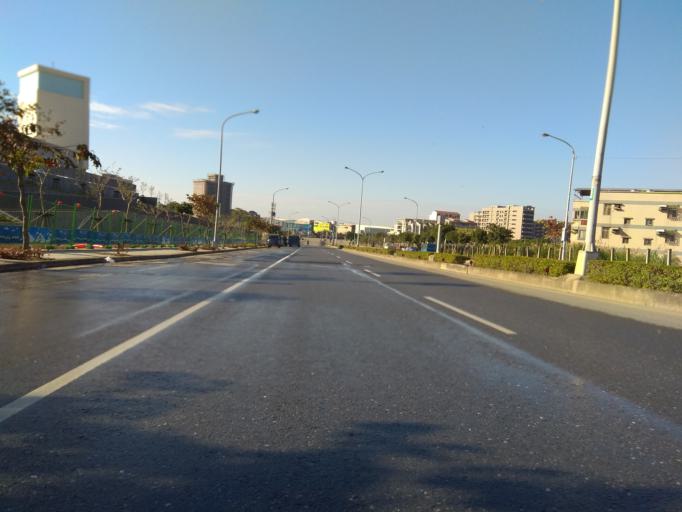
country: TW
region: Taiwan
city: Taoyuan City
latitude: 25.0177
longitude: 121.2174
